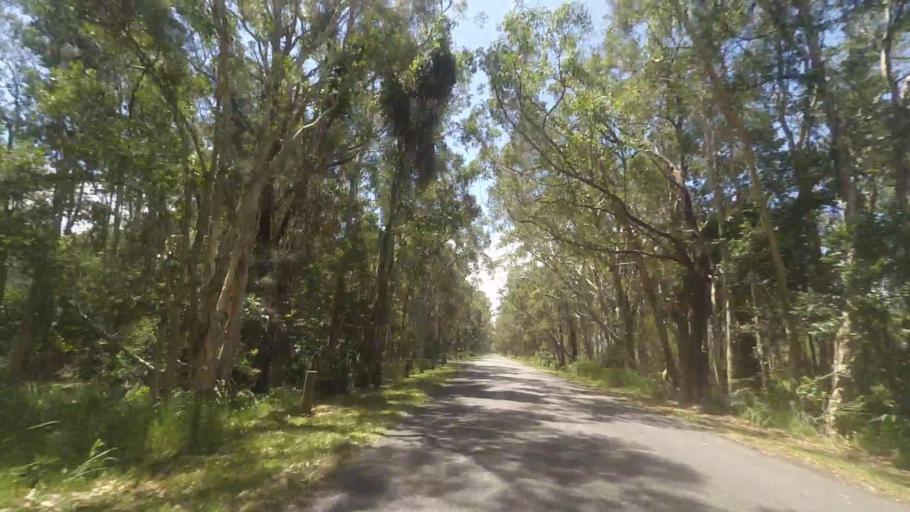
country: AU
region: New South Wales
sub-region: Great Lakes
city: Bulahdelah
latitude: -32.5286
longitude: 152.3229
